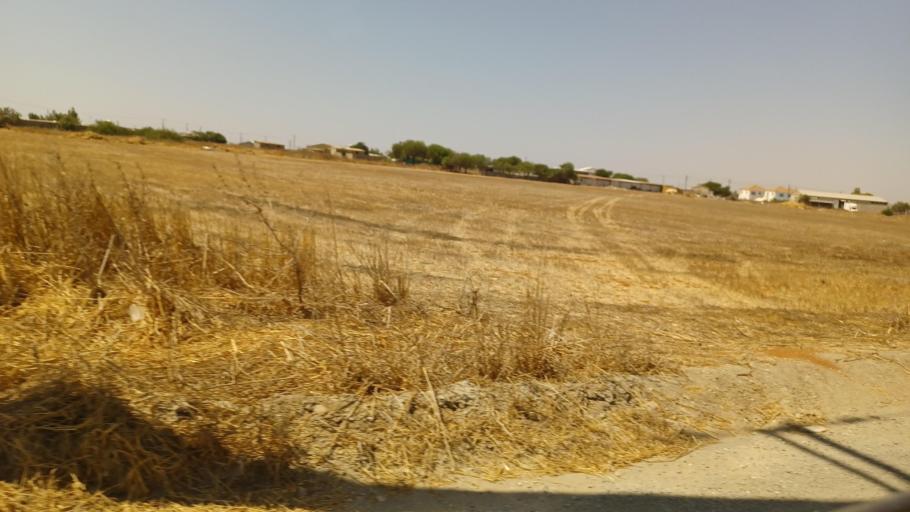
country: CY
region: Ammochostos
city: Acheritou
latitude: 35.0723
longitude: 33.8893
